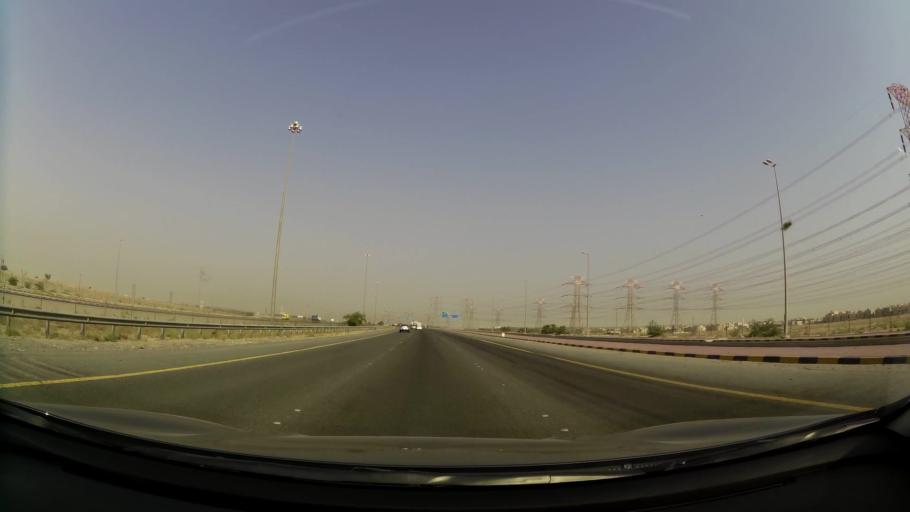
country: KW
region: Al Asimah
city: Ar Rabiyah
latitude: 29.2393
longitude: 47.8811
